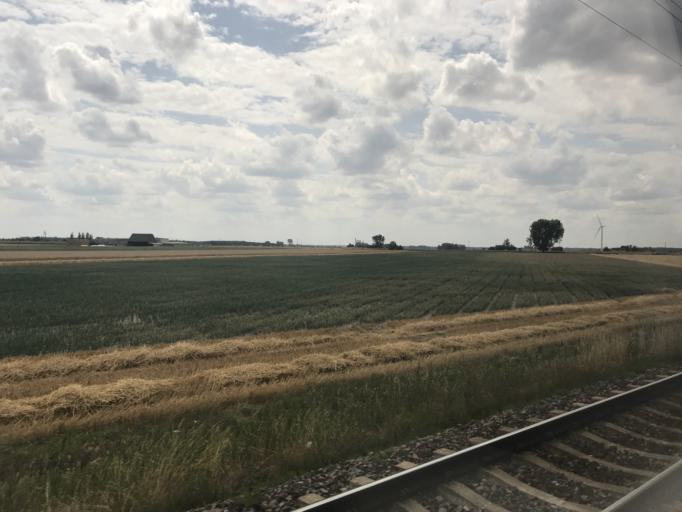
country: PL
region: Greater Poland Voivodeship
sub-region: Powiat poznanski
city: Buk
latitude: 52.3357
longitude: 16.4951
